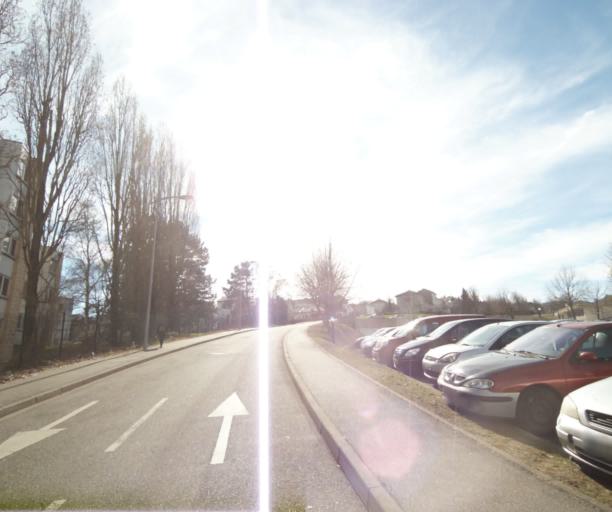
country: FR
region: Lorraine
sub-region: Departement de Meurthe-et-Moselle
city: Villers-les-Nancy
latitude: 48.6651
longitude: 6.1617
